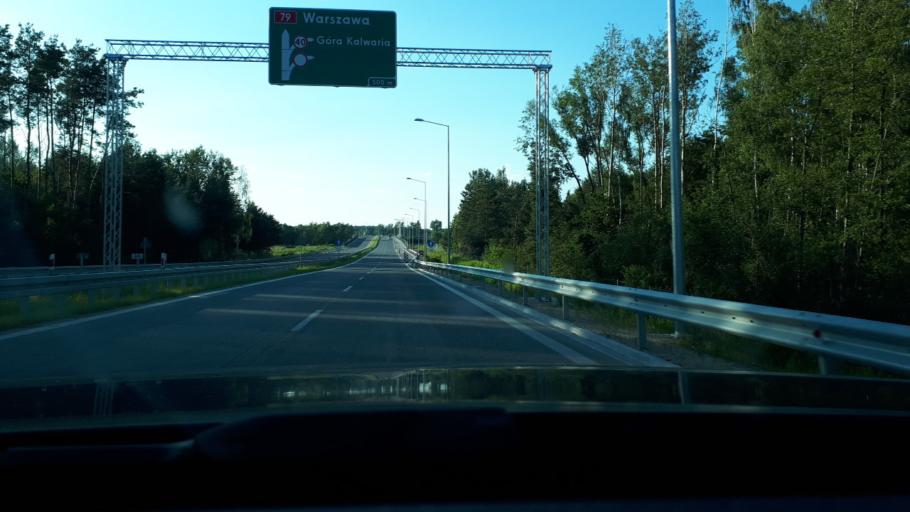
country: PL
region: Masovian Voivodeship
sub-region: Powiat piaseczynski
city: Baniocha
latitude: 51.9959
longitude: 21.1697
